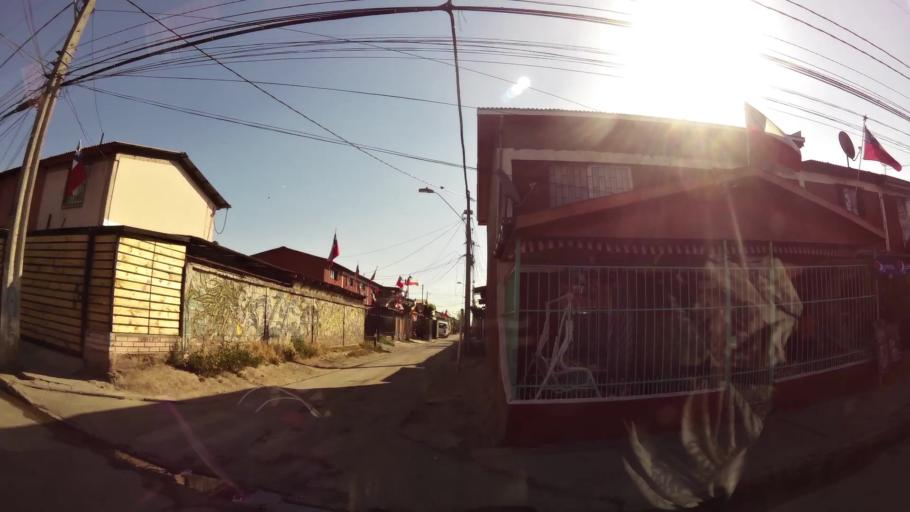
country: CL
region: Santiago Metropolitan
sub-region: Provincia de Santiago
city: La Pintana
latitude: -33.5602
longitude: -70.6074
